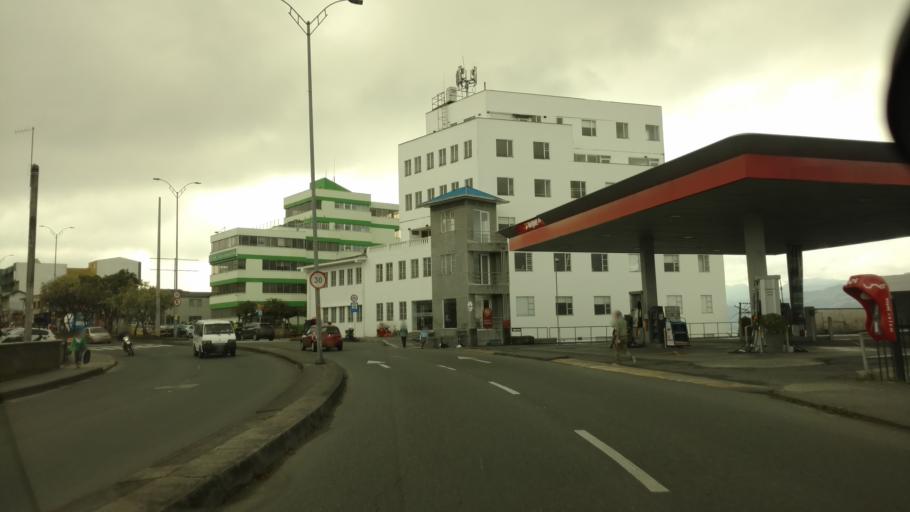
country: CO
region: Caldas
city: Manizales
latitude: 5.0663
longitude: -75.5070
